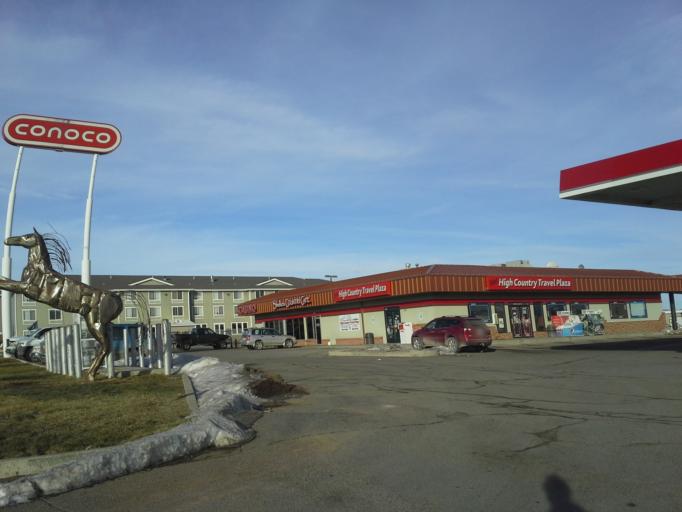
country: US
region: Montana
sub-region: Lewis and Clark County
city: Helena
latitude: 46.5914
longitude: -111.9836
